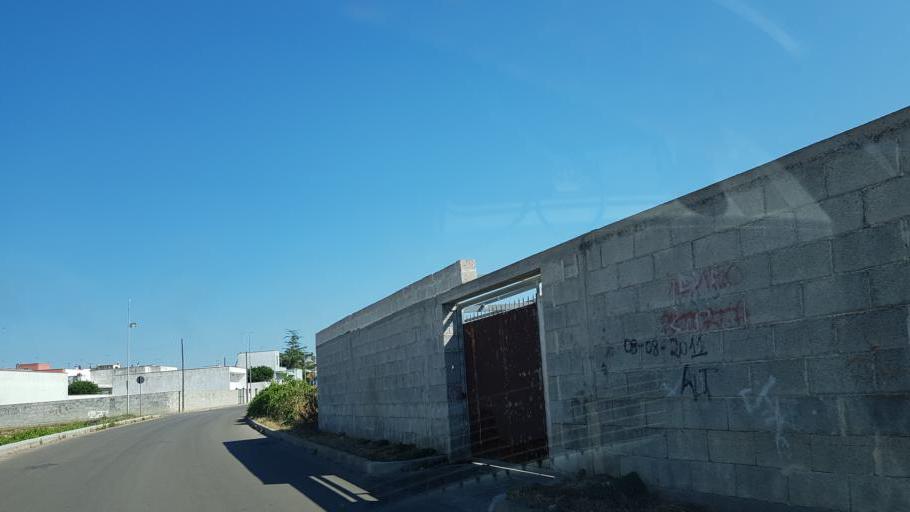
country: IT
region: Apulia
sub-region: Provincia di Brindisi
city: San Donaci
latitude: 40.4440
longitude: 17.9235
